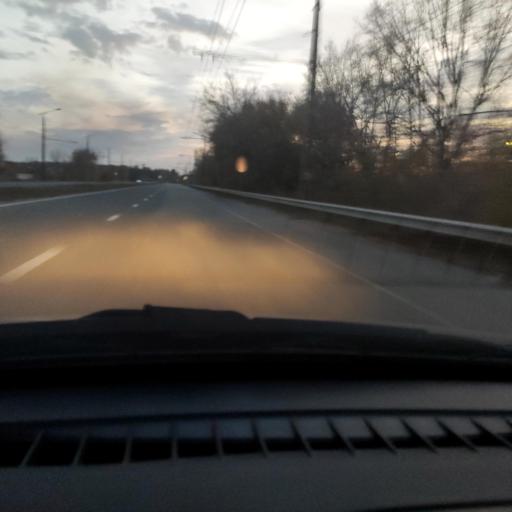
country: RU
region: Samara
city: Zhigulevsk
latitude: 53.5373
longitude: 49.5636
